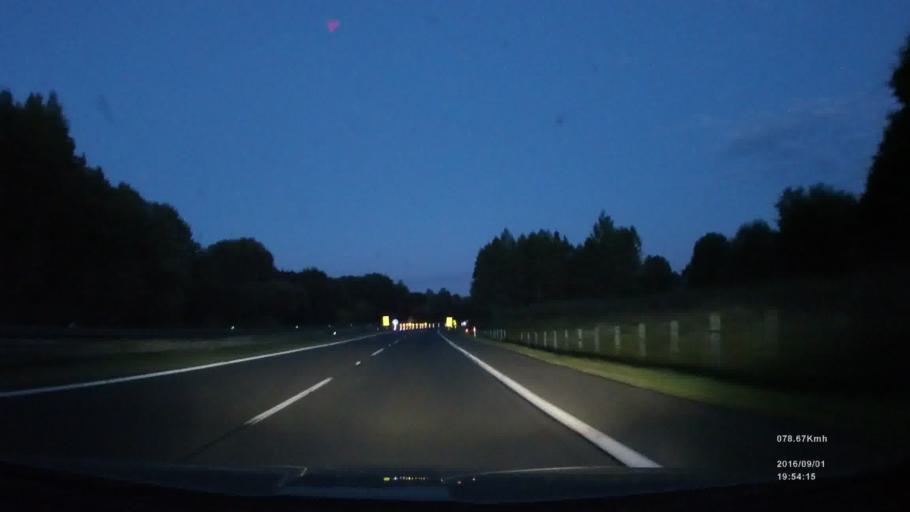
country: SK
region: Zilinsky
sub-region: Okres Liptovsky Mikulas
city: Liptovsky Mikulas
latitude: 49.0914
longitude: 19.5236
